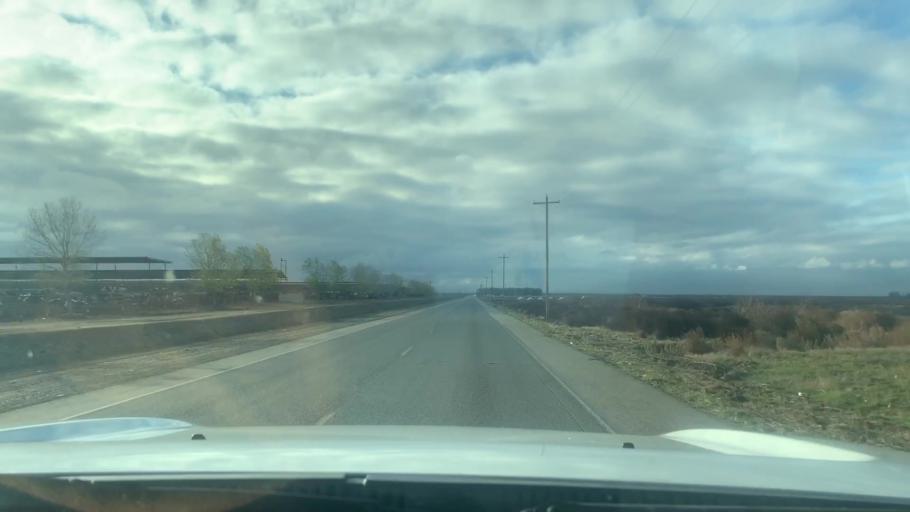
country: US
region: California
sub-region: Kern County
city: Buttonwillow
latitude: 35.5005
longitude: -119.4510
